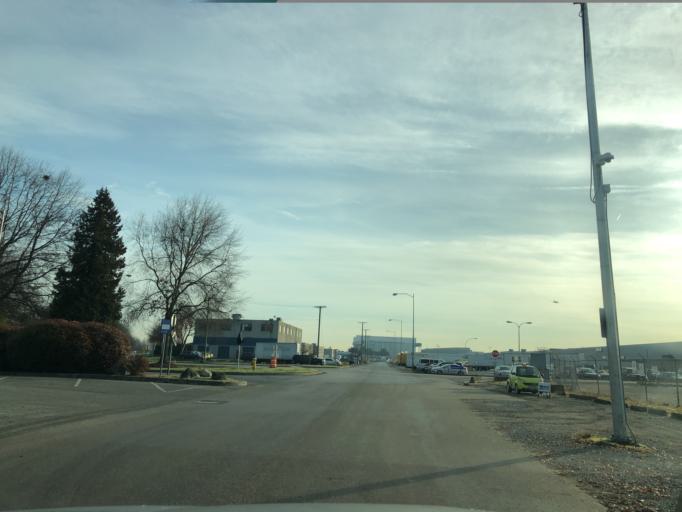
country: CA
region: British Columbia
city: Richmond
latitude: 49.1912
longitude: -123.1762
